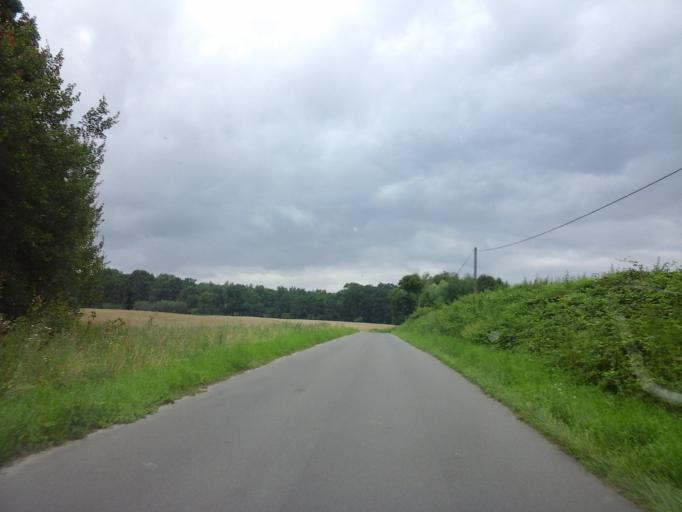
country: PL
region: West Pomeranian Voivodeship
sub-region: Powiat choszczenski
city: Krzecin
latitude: 53.0449
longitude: 15.4622
